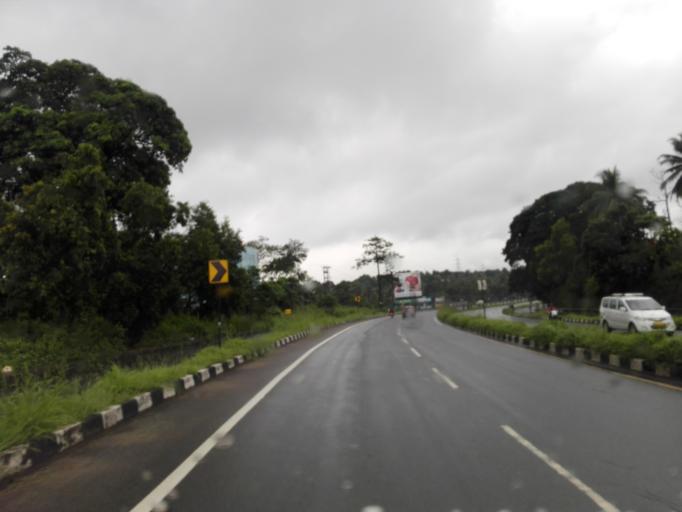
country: IN
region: Kerala
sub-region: Ernakulam
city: Elur
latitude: 10.0711
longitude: 76.3187
